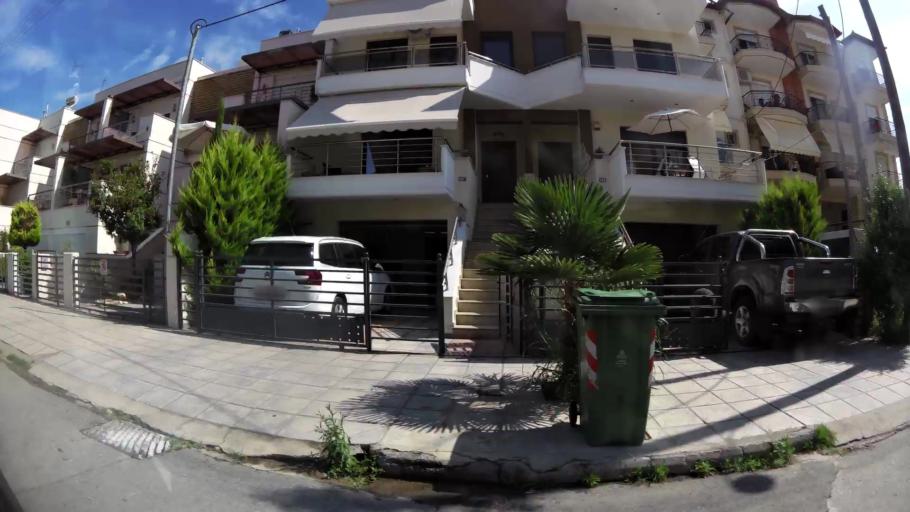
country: GR
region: Central Macedonia
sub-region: Nomos Pierias
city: Katerini
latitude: 40.2749
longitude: 22.4859
